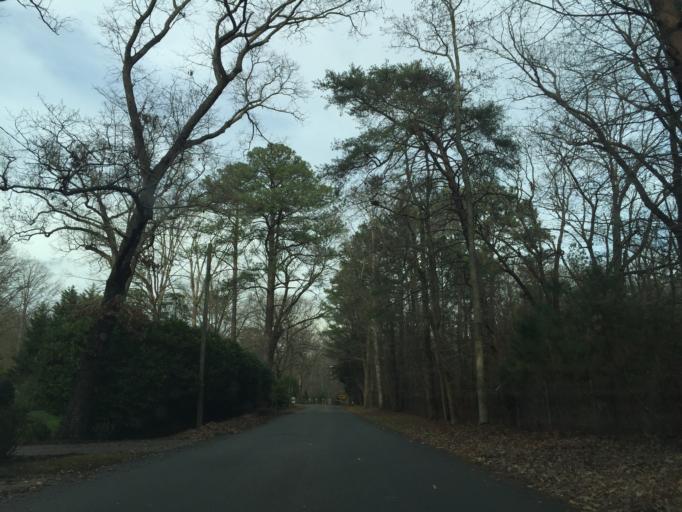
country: US
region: Virginia
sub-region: City of Newport News
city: Newport News
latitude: 37.0466
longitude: -76.4894
